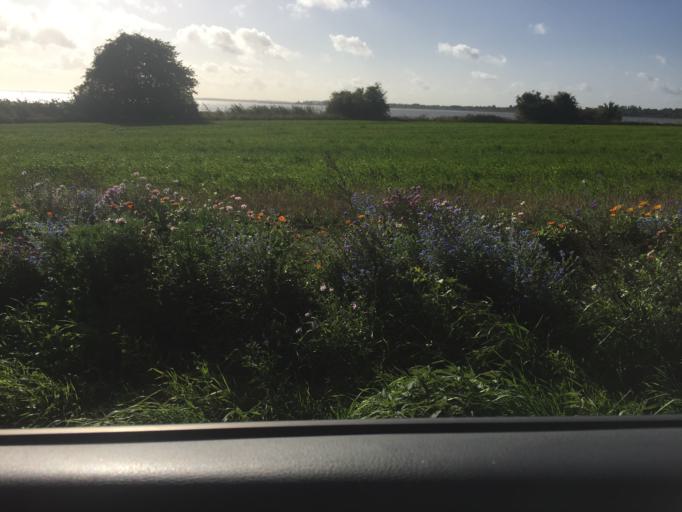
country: DK
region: Zealand
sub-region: Lolland Kommune
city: Maribo
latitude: 54.9119
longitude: 11.4928
